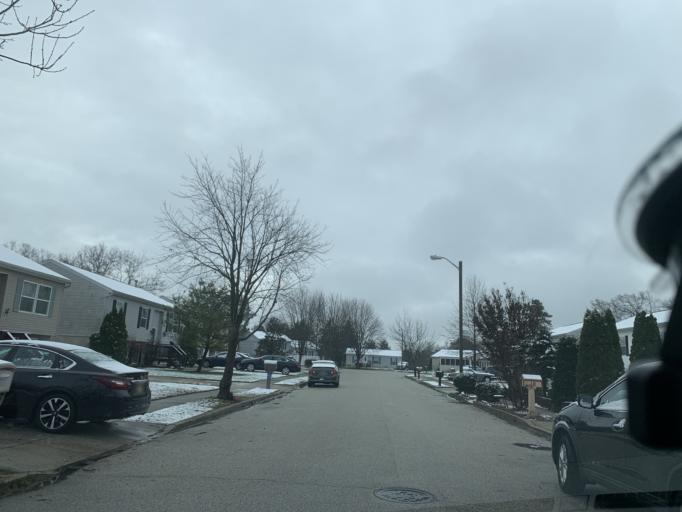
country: US
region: New Jersey
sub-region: Atlantic County
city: Pomona
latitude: 39.4329
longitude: -74.5876
